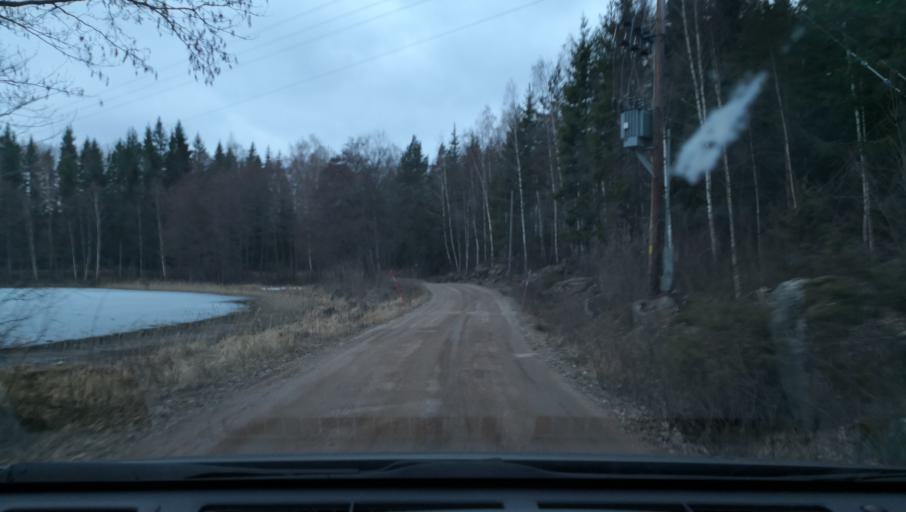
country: SE
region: OErebro
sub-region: Lindesbergs Kommun
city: Fellingsbro
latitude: 59.5770
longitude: 15.5672
